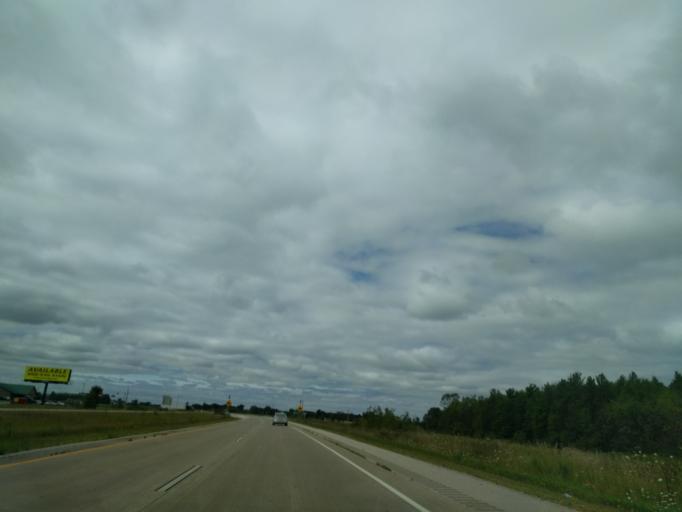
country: US
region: Wisconsin
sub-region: Marinette County
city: Peshtigo
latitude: 45.0516
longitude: -87.7951
